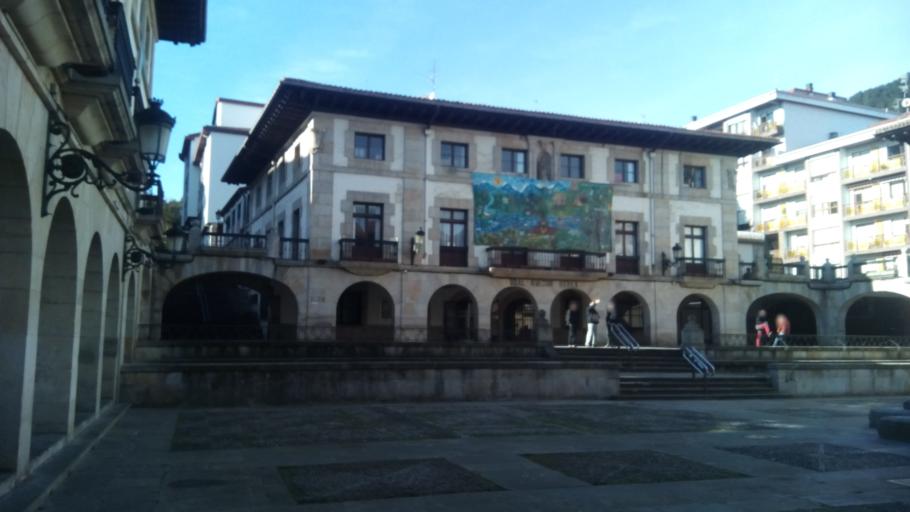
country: ES
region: Basque Country
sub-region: Bizkaia
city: Gernika-Lumo
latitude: 43.3150
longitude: -2.6783
